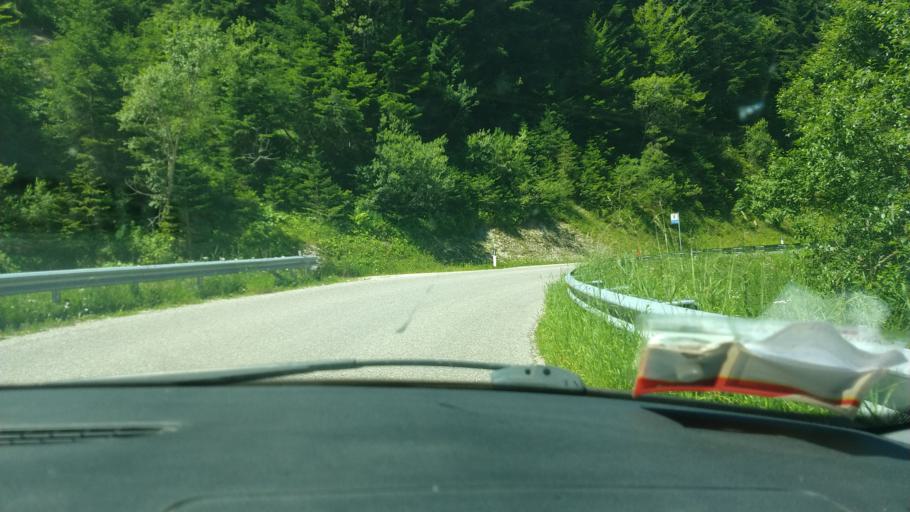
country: IT
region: Veneto
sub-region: Provincia di Vicenza
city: Lastebasse
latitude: 45.9043
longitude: 11.2214
